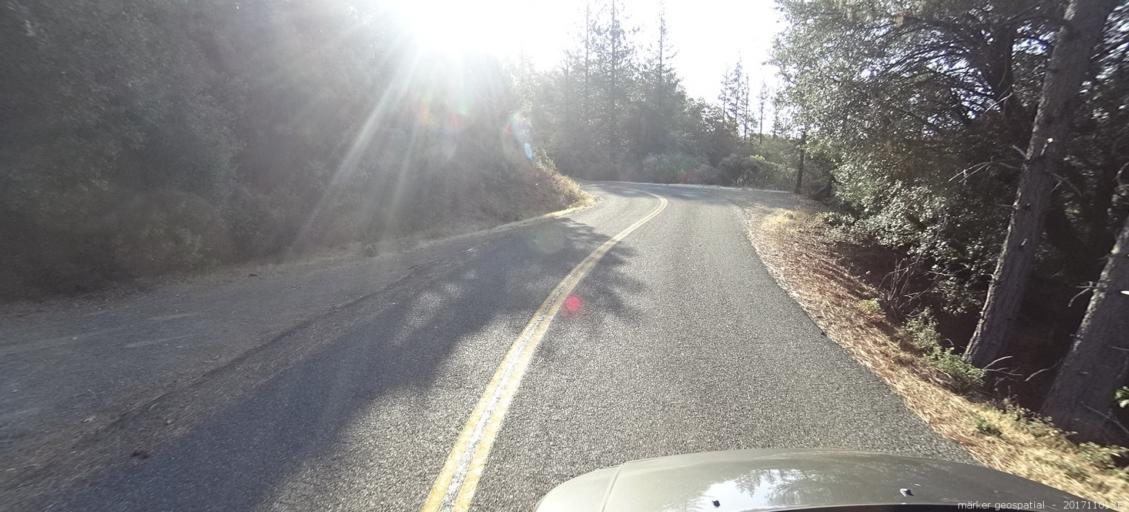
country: US
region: California
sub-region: Shasta County
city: Shasta Lake
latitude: 40.8045
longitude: -122.3087
